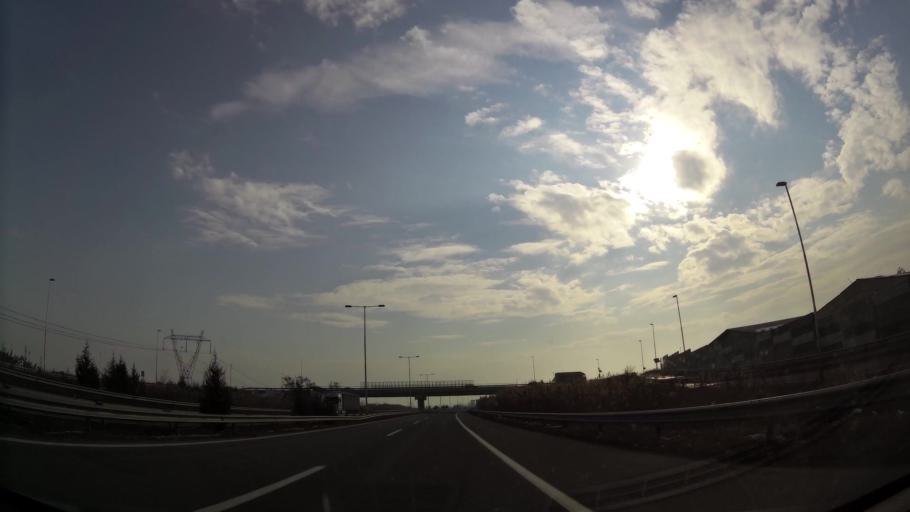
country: MK
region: Aracinovo
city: Arachinovo
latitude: 42.0191
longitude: 21.5335
